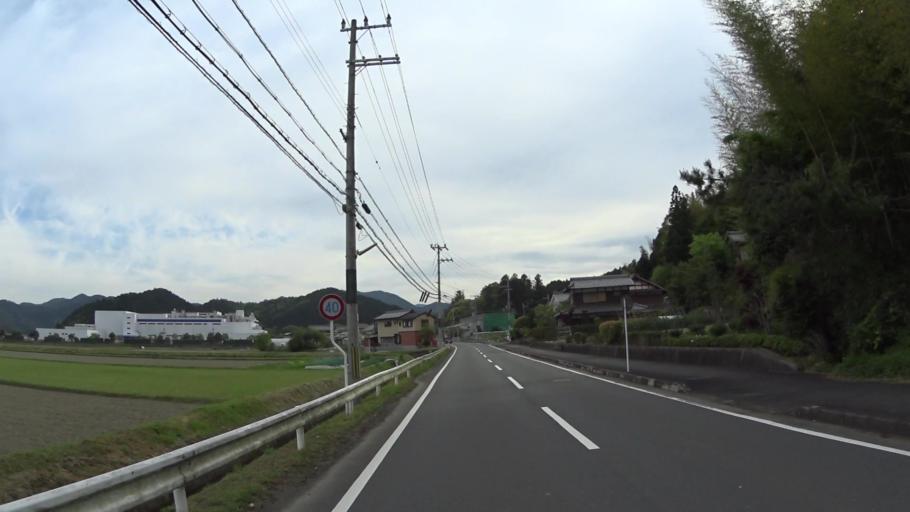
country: JP
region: Kyoto
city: Kameoka
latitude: 35.0990
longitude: 135.5090
